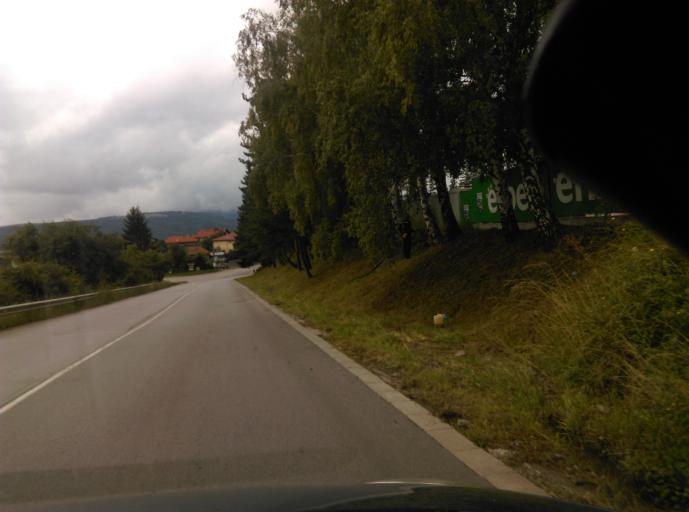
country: BG
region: Sofia-Capital
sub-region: Stolichna Obshtina
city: Sofia
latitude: 42.5917
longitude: 23.3638
